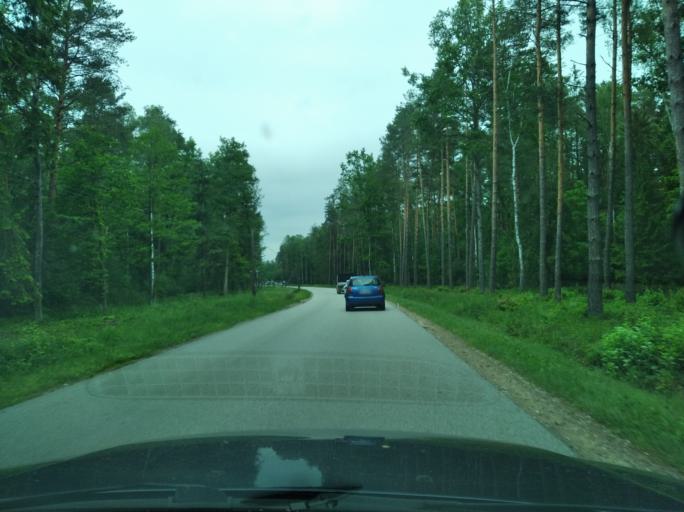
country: PL
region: Subcarpathian Voivodeship
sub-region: Powiat ropczycko-sedziszowski
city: Sedziszow Malopolski
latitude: 50.1286
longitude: 21.6716
